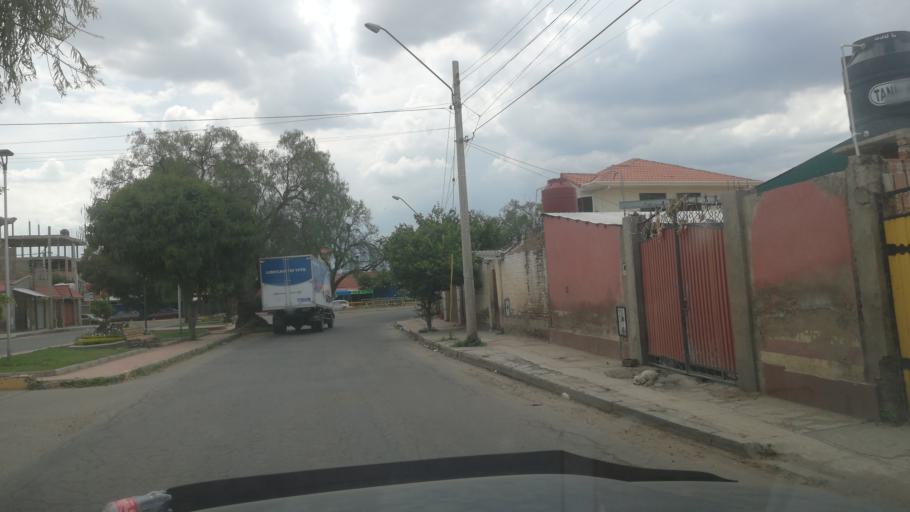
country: BO
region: Cochabamba
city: Cochabamba
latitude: -17.4055
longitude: -66.1747
